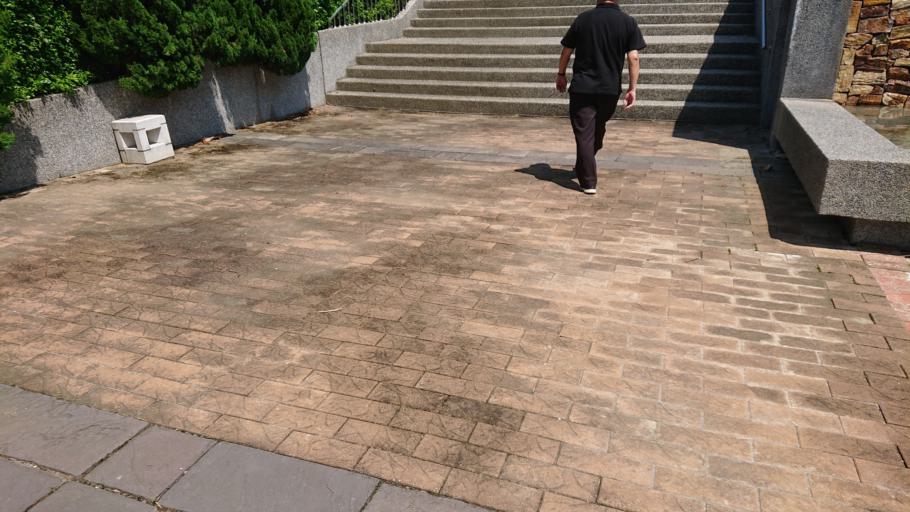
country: TW
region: Taiwan
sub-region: Hsinchu
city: Hsinchu
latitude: 24.7879
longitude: 120.9700
